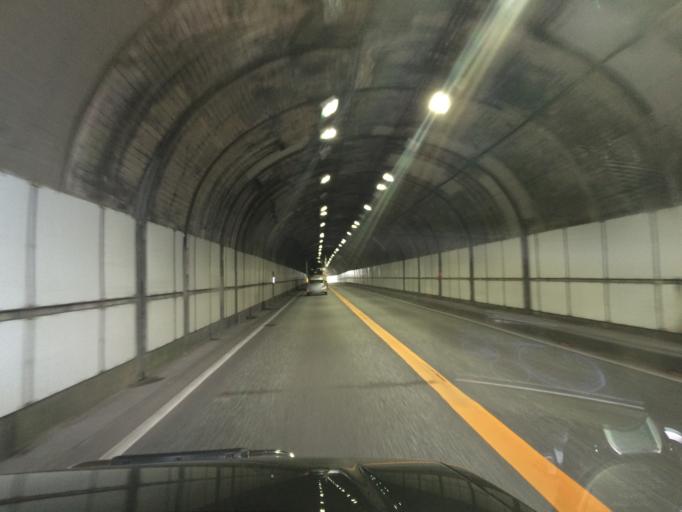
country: JP
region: Hyogo
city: Toyooka
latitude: 35.3524
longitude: 134.8346
